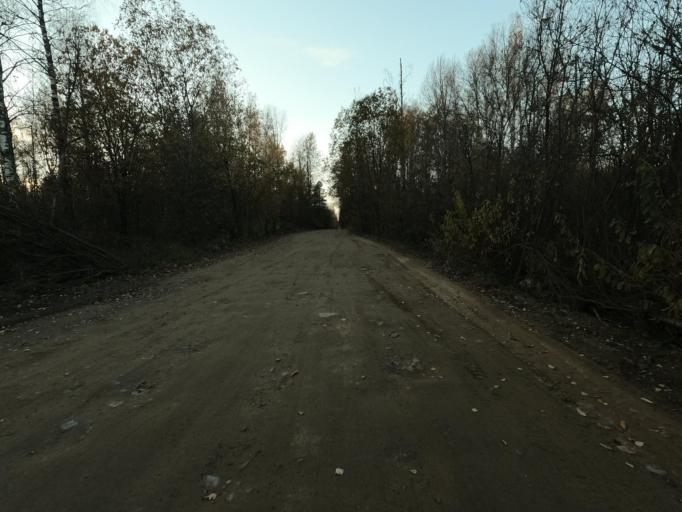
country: RU
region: Leningrad
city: Mga
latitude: 59.7572
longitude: 31.2726
